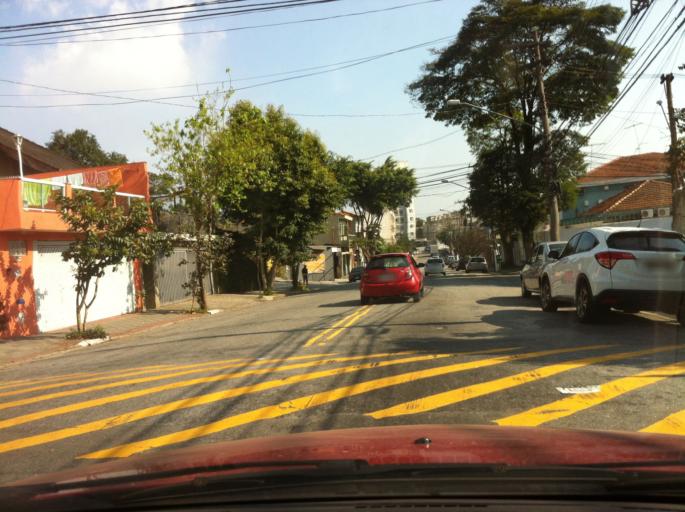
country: BR
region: Sao Paulo
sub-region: Diadema
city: Diadema
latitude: -23.6316
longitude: -46.6434
